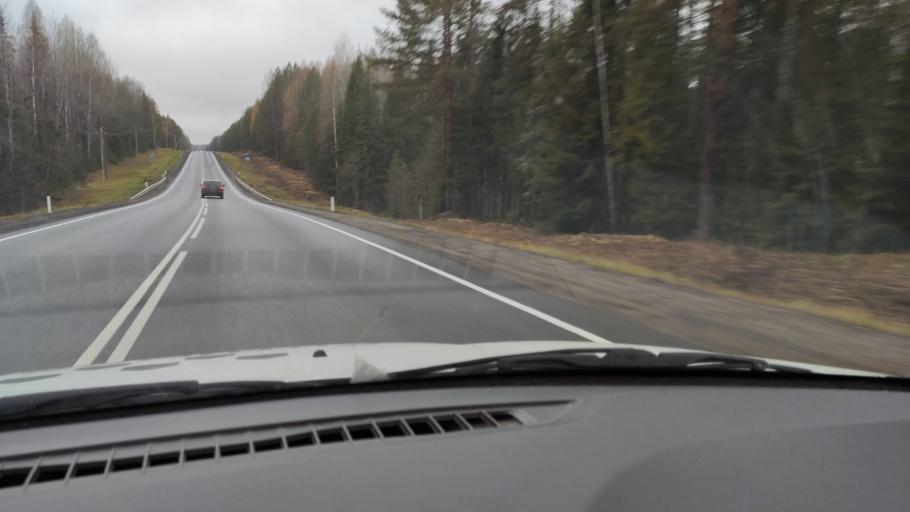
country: RU
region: Kirov
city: Dubrovka
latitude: 58.9139
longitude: 51.1621
